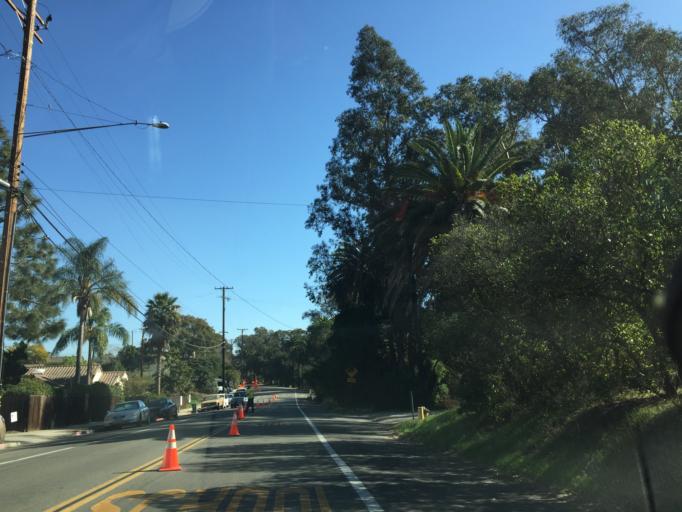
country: US
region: California
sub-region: Santa Barbara County
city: Mission Canyon
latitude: 34.4387
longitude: -119.7678
